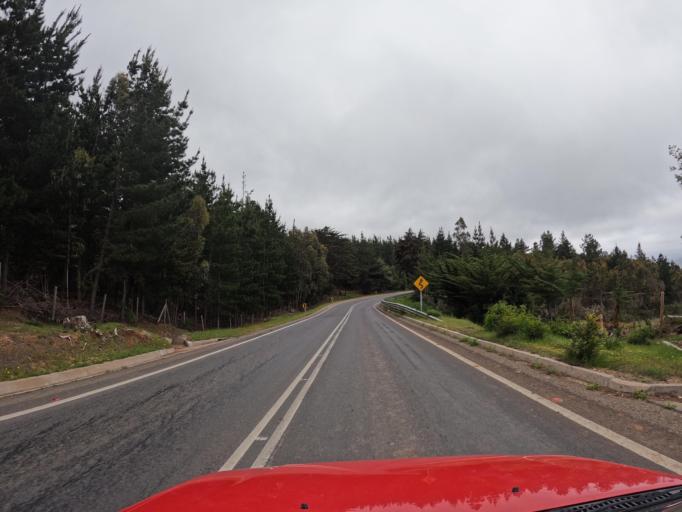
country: CL
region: O'Higgins
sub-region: Provincia de Colchagua
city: Santa Cruz
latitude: -34.5964
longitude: -72.0168
